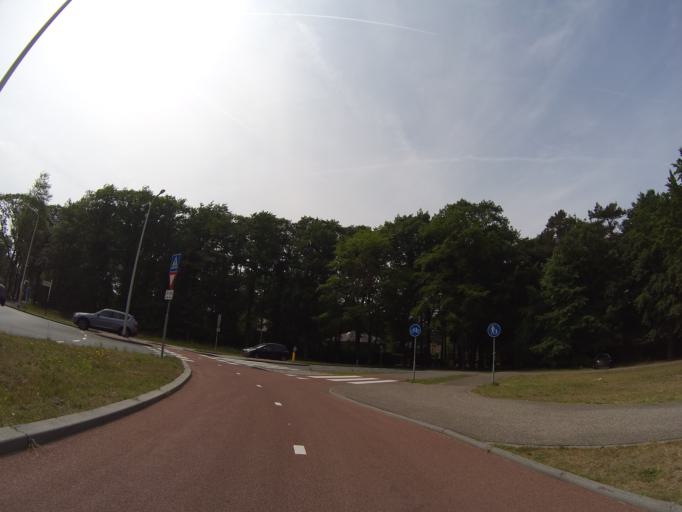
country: NL
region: Utrecht
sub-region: Gemeente Zeist
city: Zeist
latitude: 52.1011
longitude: 5.2661
